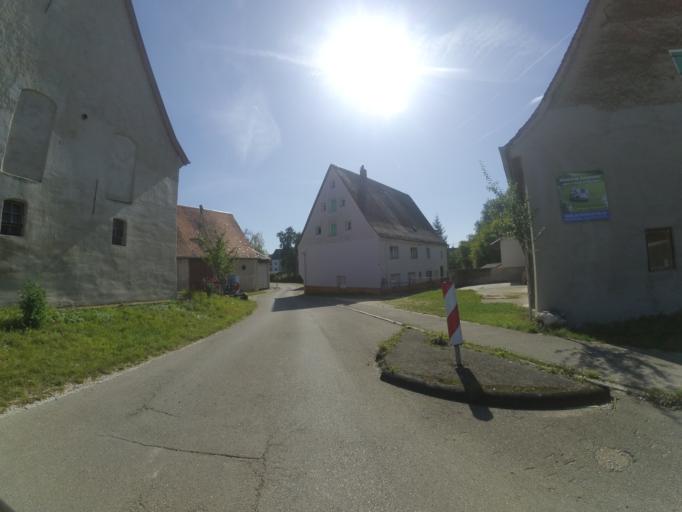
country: DE
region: Baden-Wuerttemberg
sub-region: Tuebingen Region
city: Langenau
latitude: 48.4975
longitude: 10.1119
